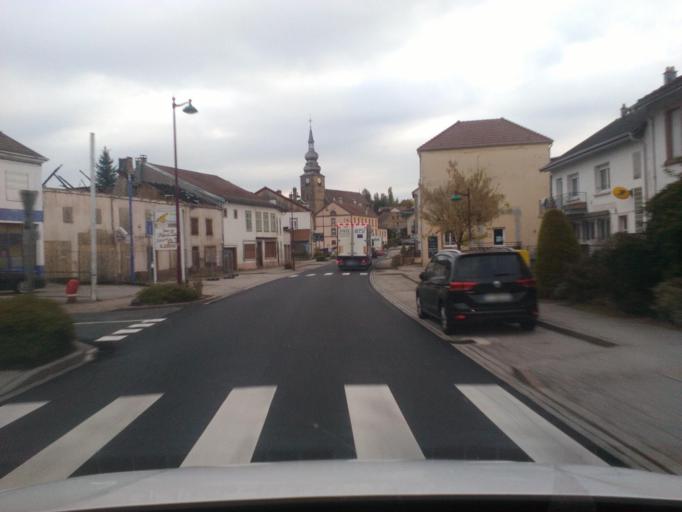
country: FR
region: Lorraine
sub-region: Departement des Vosges
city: Ban-de-Laveline
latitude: 48.3074
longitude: 7.0785
